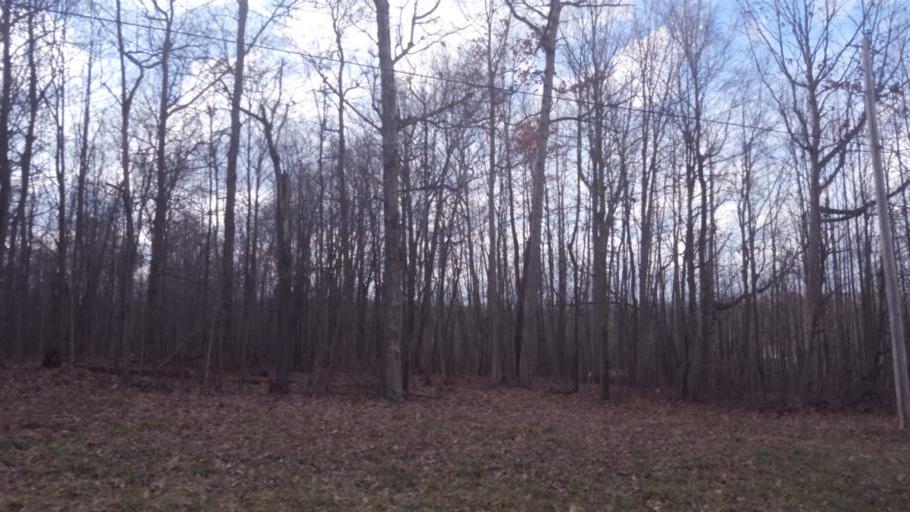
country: US
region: Ohio
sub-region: Sandusky County
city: Bellville
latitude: 40.5449
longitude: -82.4329
